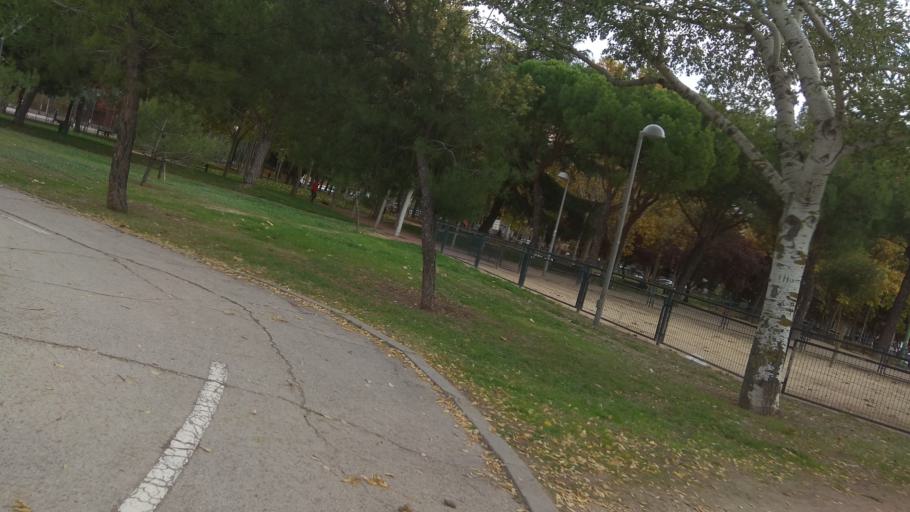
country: ES
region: Madrid
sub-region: Provincia de Madrid
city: Vicalvaro
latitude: 40.4087
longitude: -3.6160
